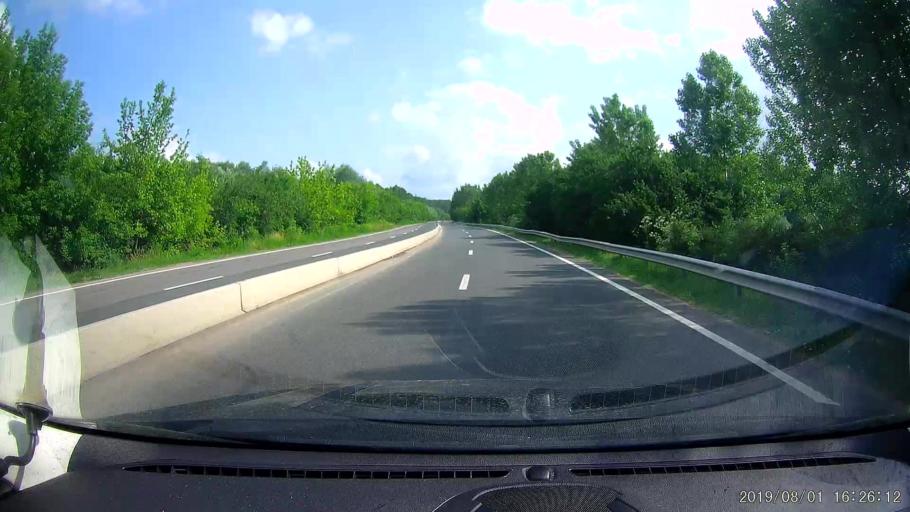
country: RO
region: Calarasi
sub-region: Municipiul Calarasi
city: Calarasi
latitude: 44.1849
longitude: 27.3217
